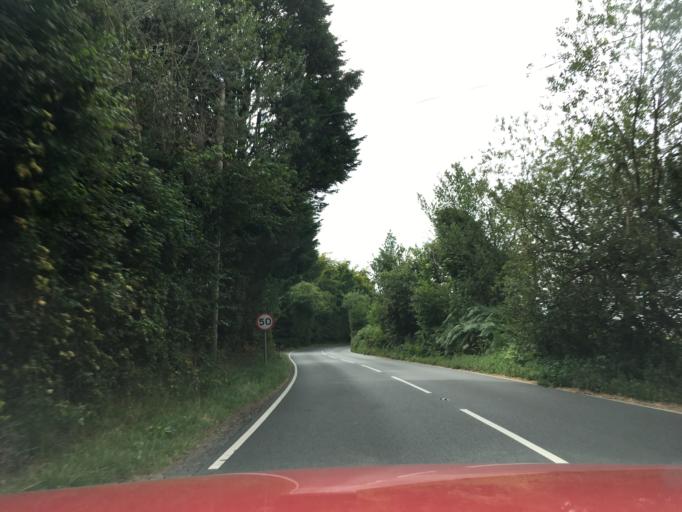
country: GB
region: England
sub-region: Kent
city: Cranbrook
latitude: 51.1111
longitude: 0.5106
